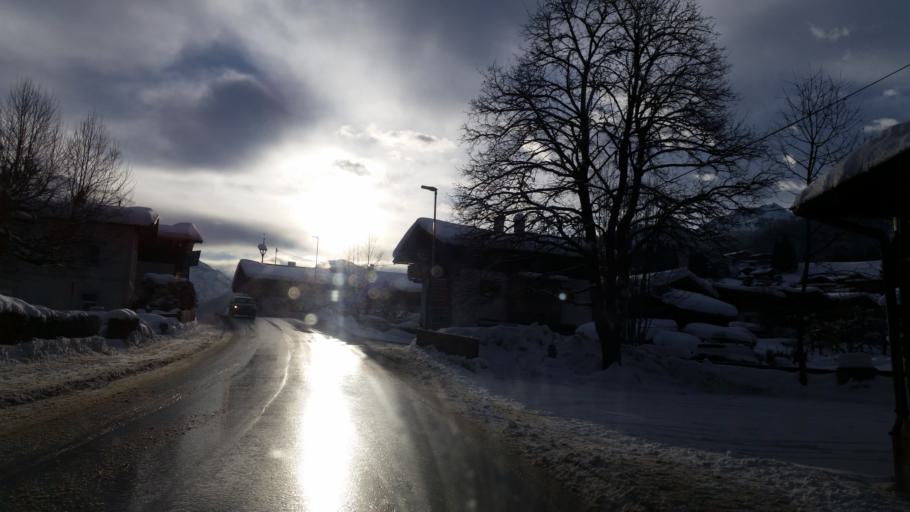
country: AT
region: Tyrol
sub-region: Politischer Bezirk Kitzbuhel
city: Fieberbrunn
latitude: 47.4817
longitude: 12.5360
